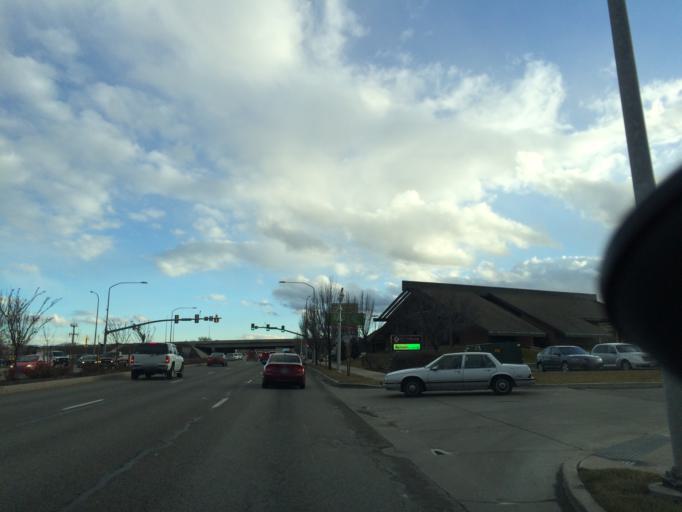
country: US
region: Utah
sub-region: Salt Lake County
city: Taylorsville
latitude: 40.6476
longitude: -111.9389
